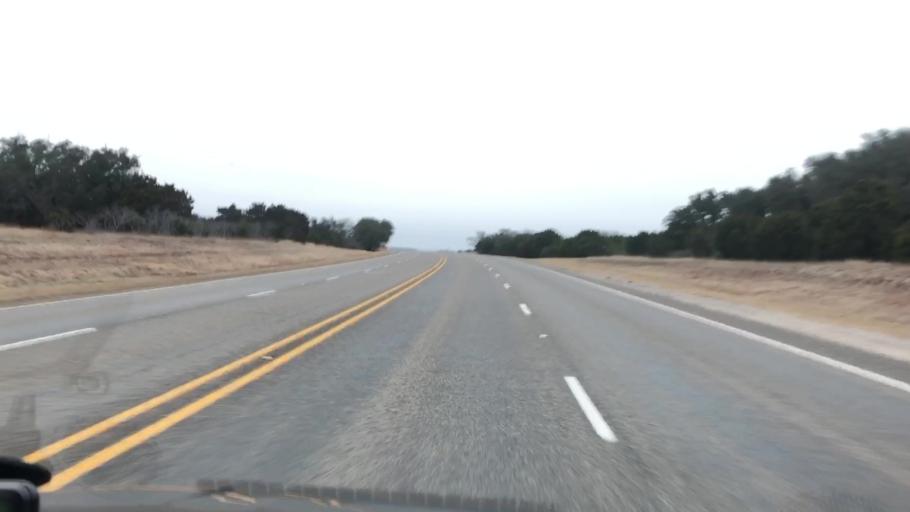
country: US
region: Texas
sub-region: Lampasas County
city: Lampasas
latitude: 31.1900
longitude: -98.1718
